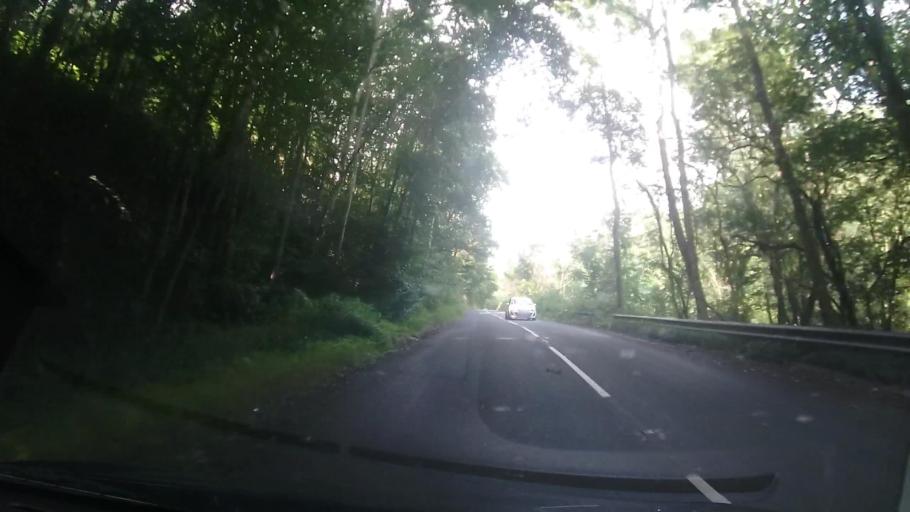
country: GB
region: Wales
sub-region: Sir Powys
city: Knighton
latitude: 52.3623
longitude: -3.0478
